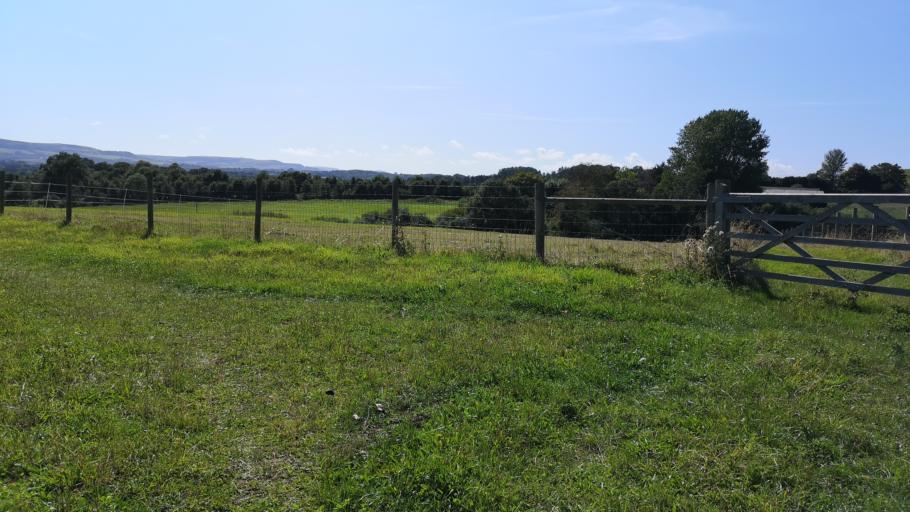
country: GB
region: England
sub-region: Isle of Wight
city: Brading
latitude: 50.6736
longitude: -1.1553
